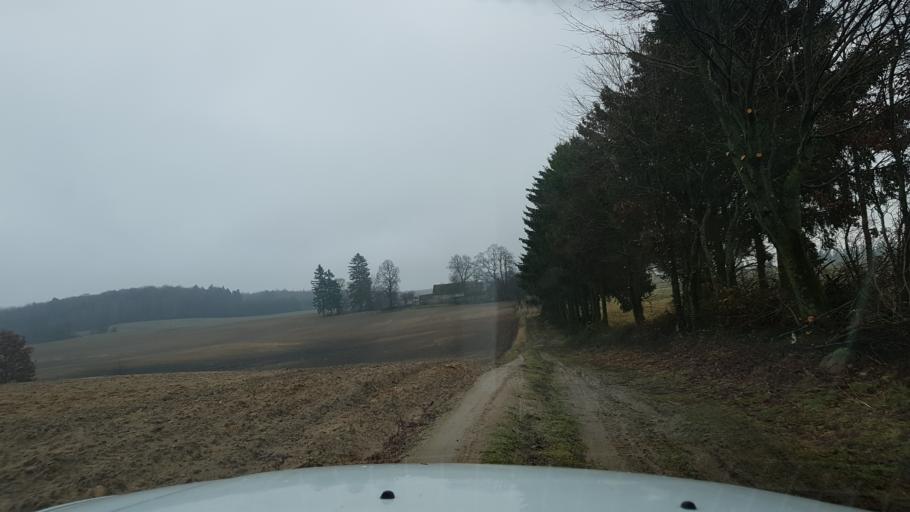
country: PL
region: West Pomeranian Voivodeship
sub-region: Powiat drawski
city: Czaplinek
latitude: 53.5788
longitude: 16.2576
